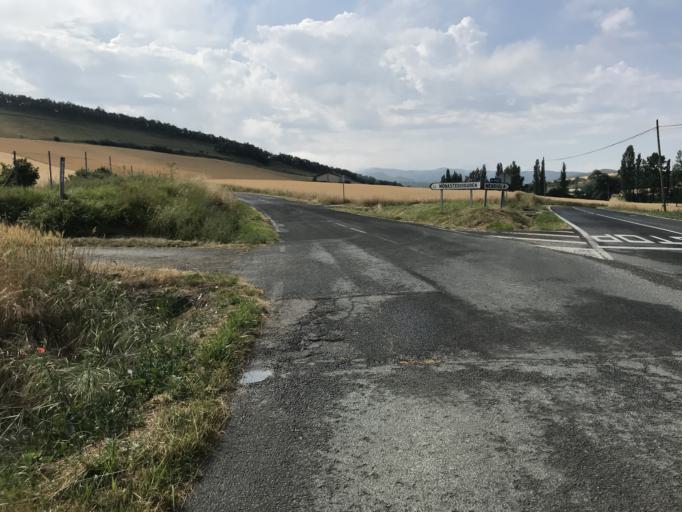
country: ES
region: Basque Country
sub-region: Provincia de Alava
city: Gasteiz / Vitoria
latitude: 42.8240
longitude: -2.6494
